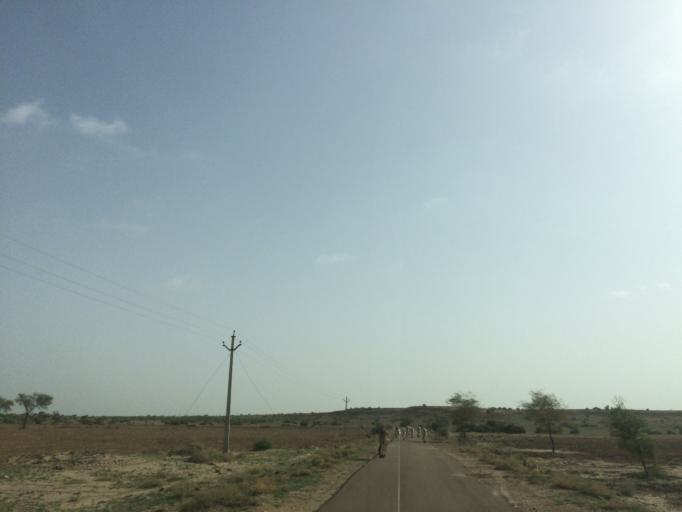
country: IN
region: Rajasthan
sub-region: Jaisalmer
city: Jaisalmer
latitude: 26.8406
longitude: 70.7473
